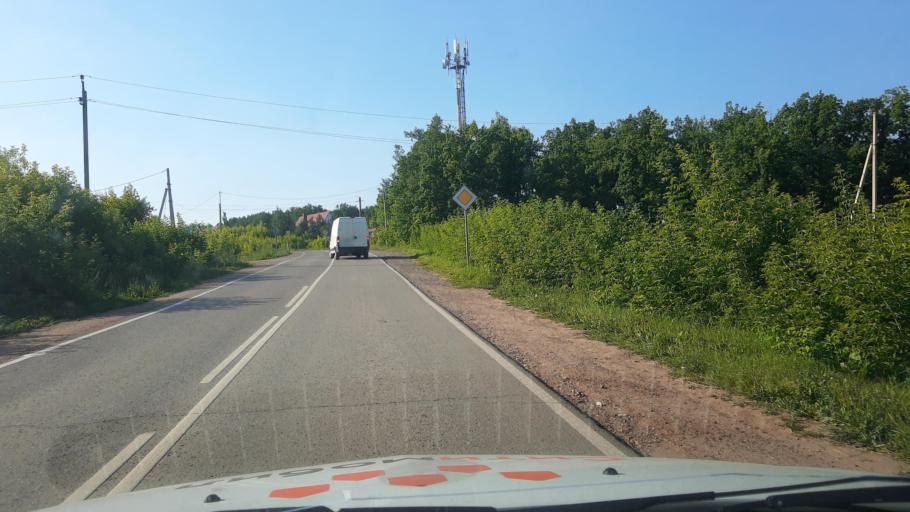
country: RU
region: Bashkortostan
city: Avdon
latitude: 54.6171
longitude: 55.6385
